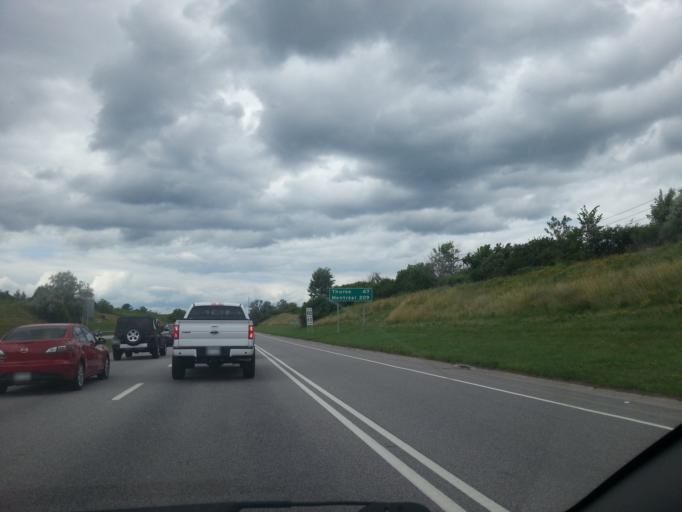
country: CA
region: Quebec
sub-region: Outaouais
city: Gatineau
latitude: 45.4775
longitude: -75.7136
